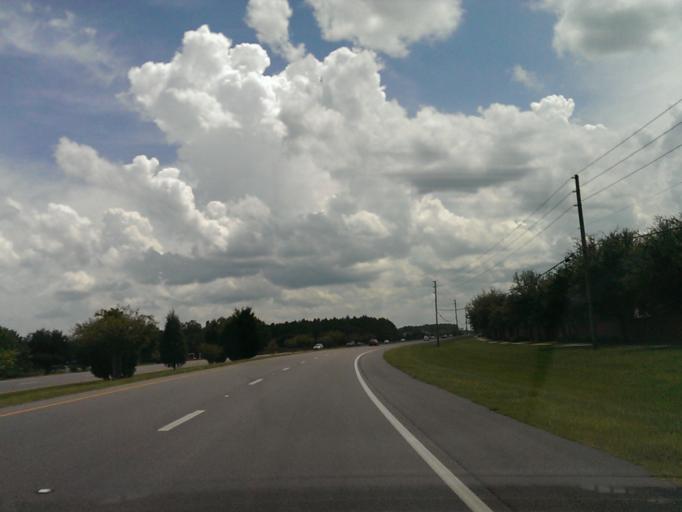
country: US
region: Florida
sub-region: Orange County
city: Bay Hill
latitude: 28.4345
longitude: -81.5334
